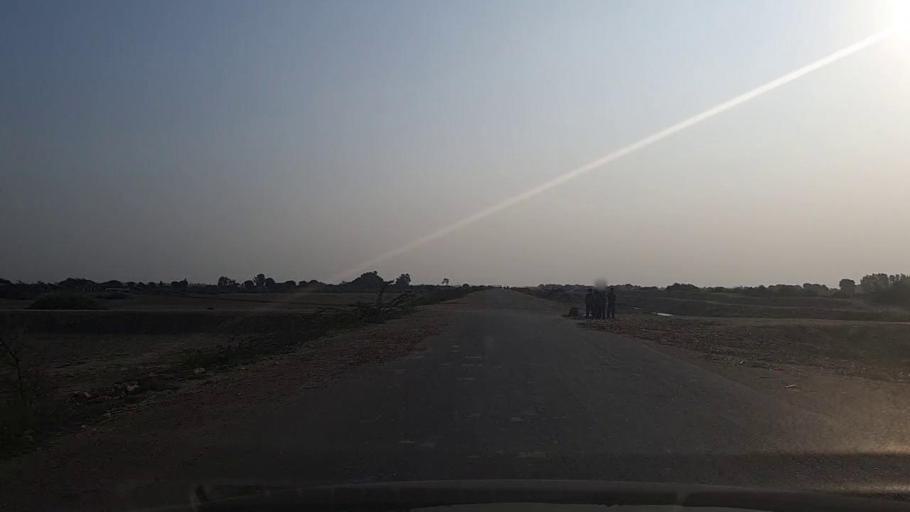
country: PK
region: Sindh
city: Mirpur Sakro
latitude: 24.4879
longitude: 67.8081
